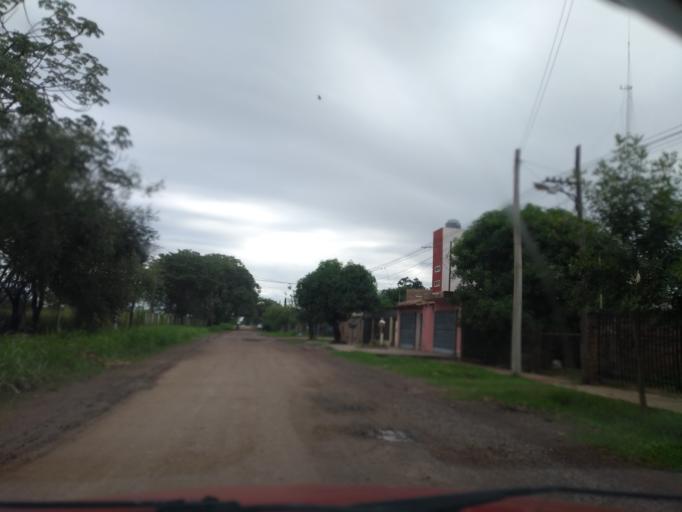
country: AR
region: Chaco
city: Barranqueras
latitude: -27.4793
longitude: -58.9608
